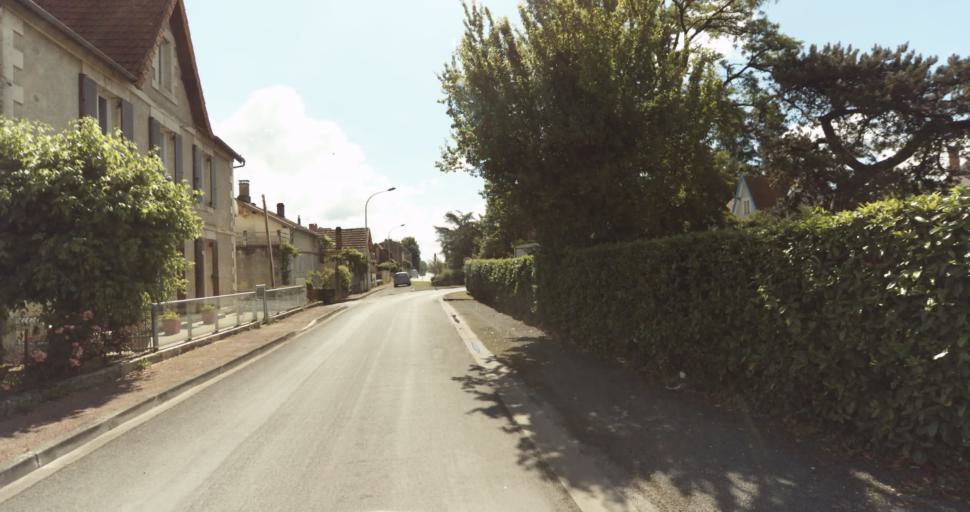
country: FR
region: Aquitaine
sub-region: Departement de la Dordogne
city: Le Bugue
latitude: 44.8469
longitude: 0.9129
